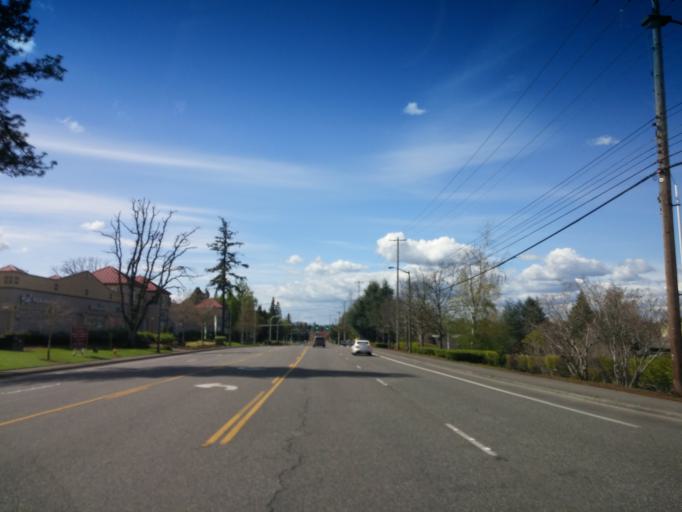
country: US
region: Oregon
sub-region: Washington County
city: Oak Hills
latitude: 45.5175
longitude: -122.8418
